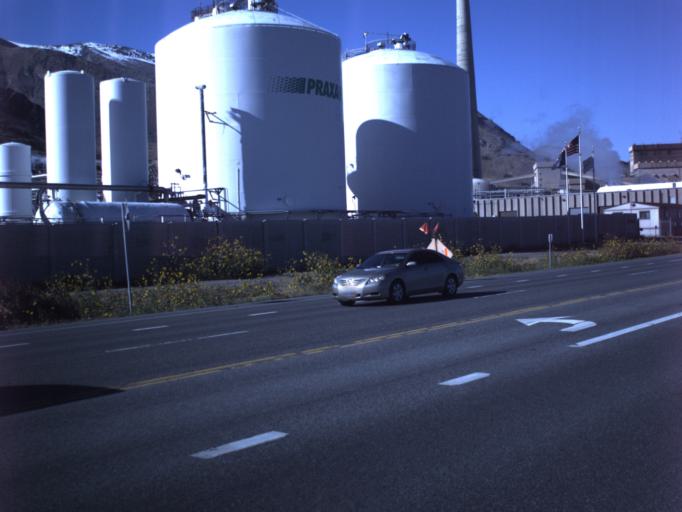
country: US
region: Utah
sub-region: Salt Lake County
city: Magna
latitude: 40.7276
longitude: -112.1857
